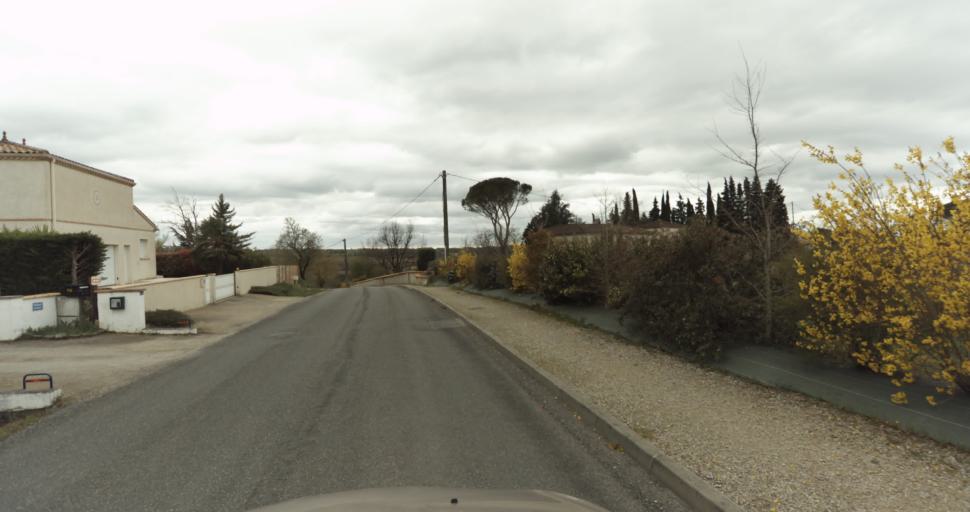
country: FR
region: Midi-Pyrenees
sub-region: Departement du Tarn
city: Puygouzon
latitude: 43.8953
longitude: 2.1721
